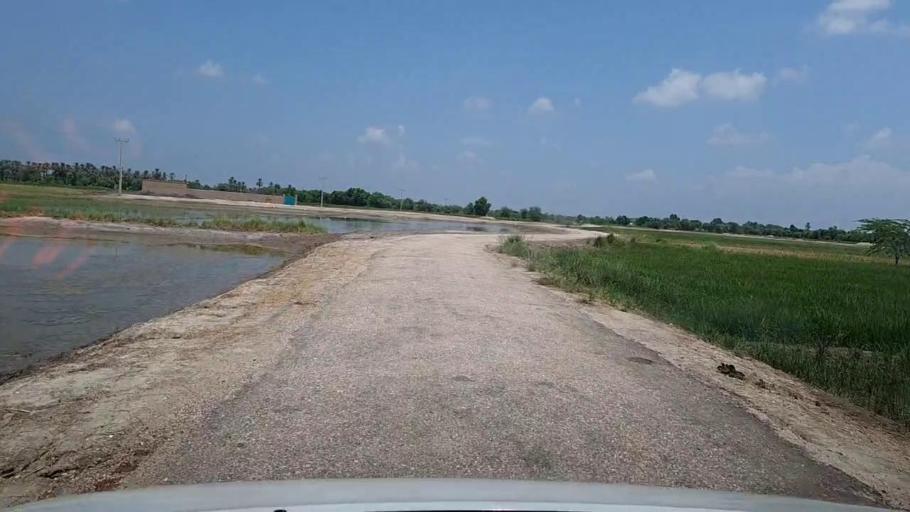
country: PK
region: Sindh
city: Kandiaro
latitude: 26.9864
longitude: 68.2321
